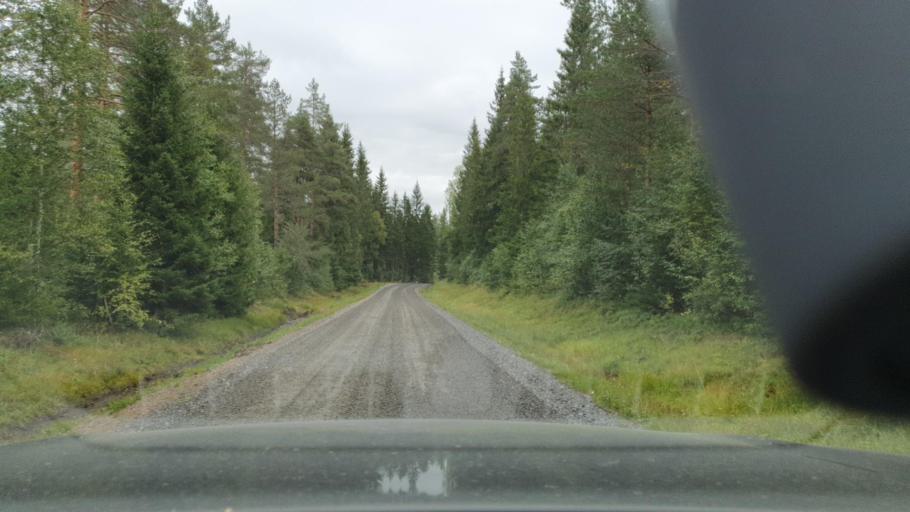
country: SE
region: Vaermland
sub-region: Torsby Kommun
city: Torsby
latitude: 60.4114
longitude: 12.6831
